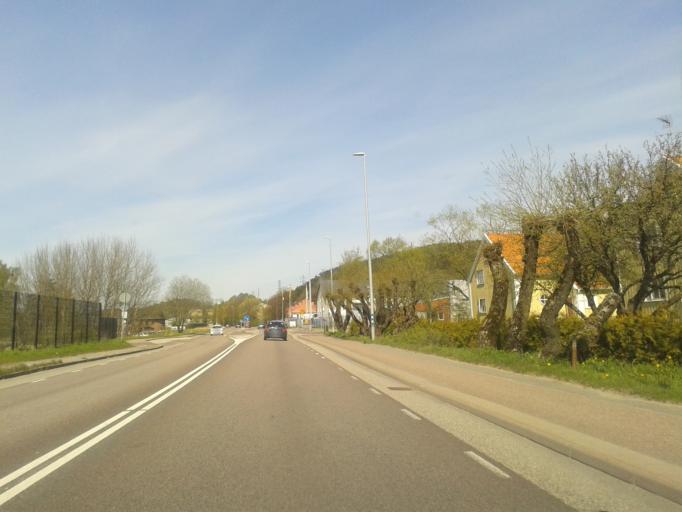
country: SE
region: Vaestra Goetaland
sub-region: Goteborg
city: Eriksbo
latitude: 57.7482
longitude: 12.0100
